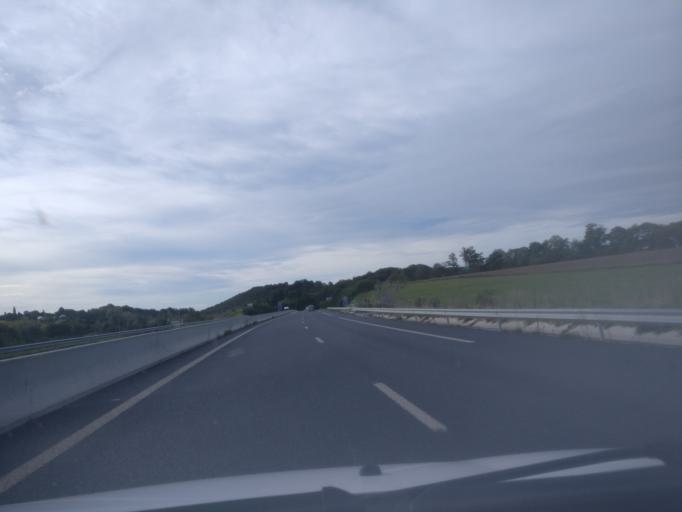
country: FR
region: Lower Normandy
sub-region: Departement de la Manche
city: Sartilly
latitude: 48.7487
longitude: -1.4420
